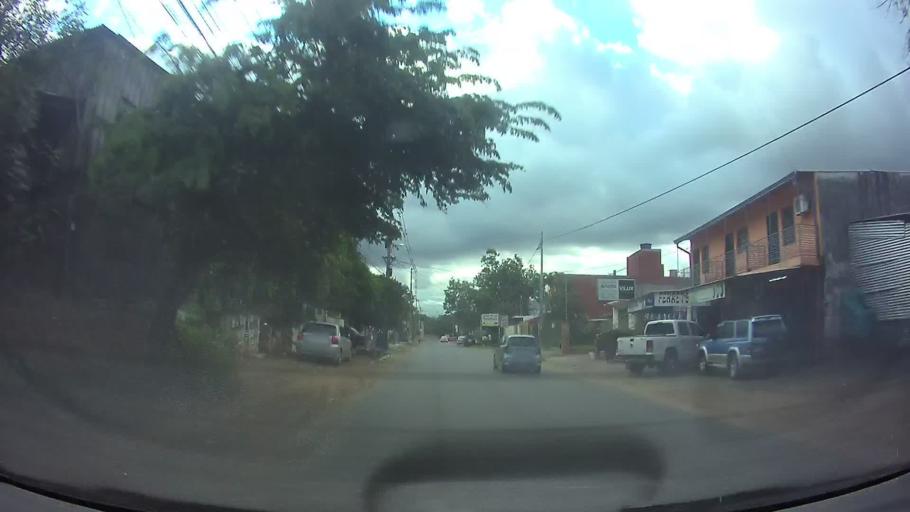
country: PY
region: Central
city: Fernando de la Mora
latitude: -25.3181
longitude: -57.5413
